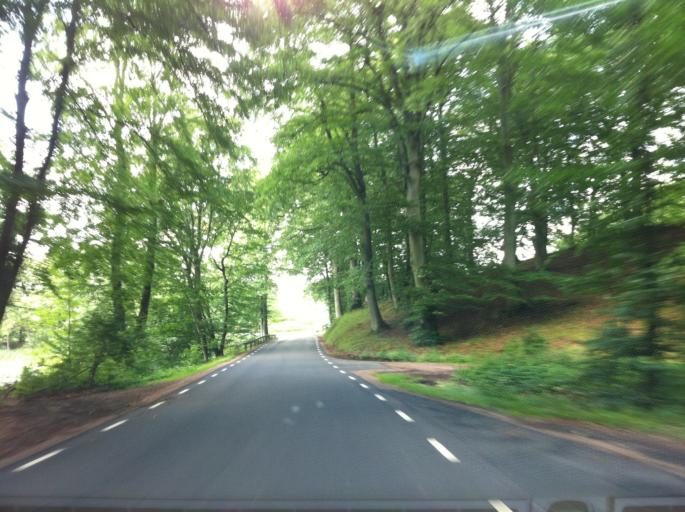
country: SE
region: Skane
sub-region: Trelleborgs Kommun
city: Anderslov
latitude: 55.4756
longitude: 13.3650
